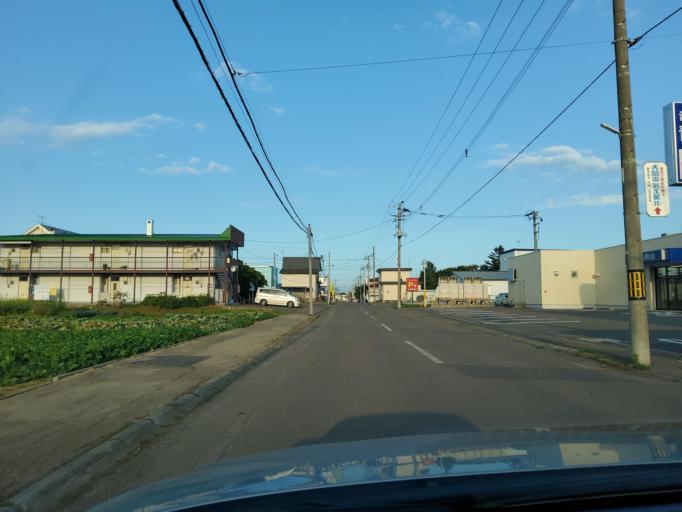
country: JP
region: Hokkaido
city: Obihiro
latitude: 42.9316
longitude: 143.1882
